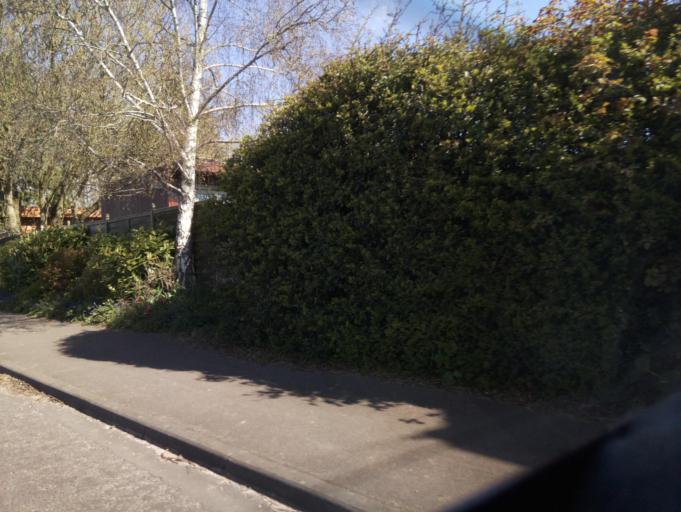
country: GB
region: England
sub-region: Wiltshire
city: Bradford-on-Avon
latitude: 51.3342
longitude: -2.2379
